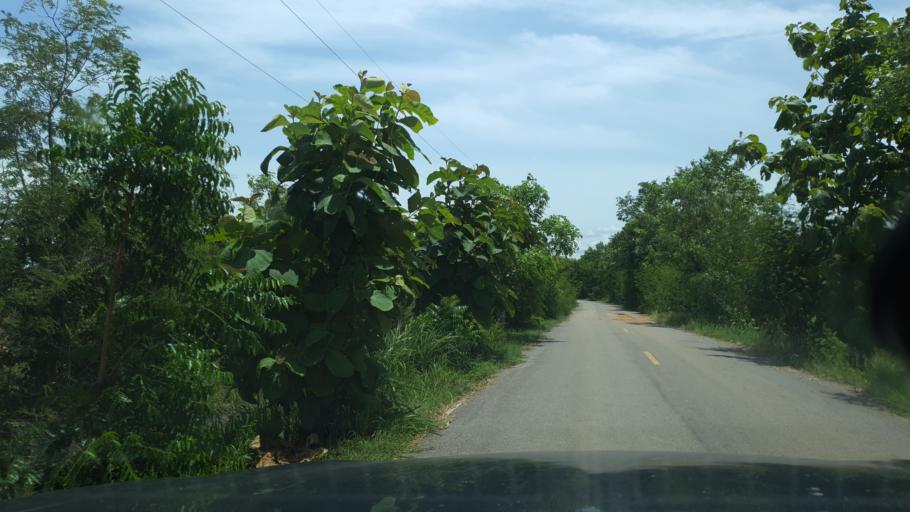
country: TH
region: Sukhothai
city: Ban Na
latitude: 17.1269
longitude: 99.6727
